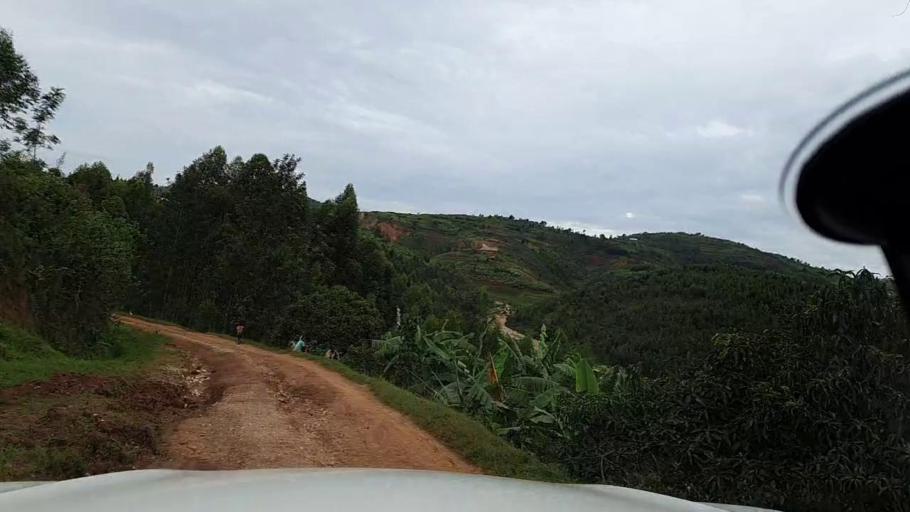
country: RW
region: Southern Province
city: Gitarama
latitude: -2.0916
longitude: 29.6383
